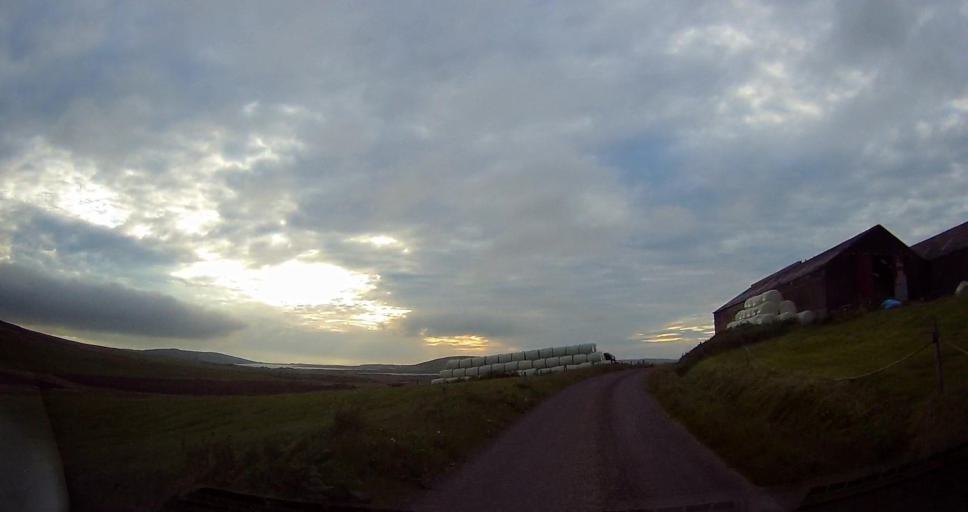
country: GB
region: Scotland
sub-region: Orkney Islands
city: Stromness
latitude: 59.1017
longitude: -3.2097
